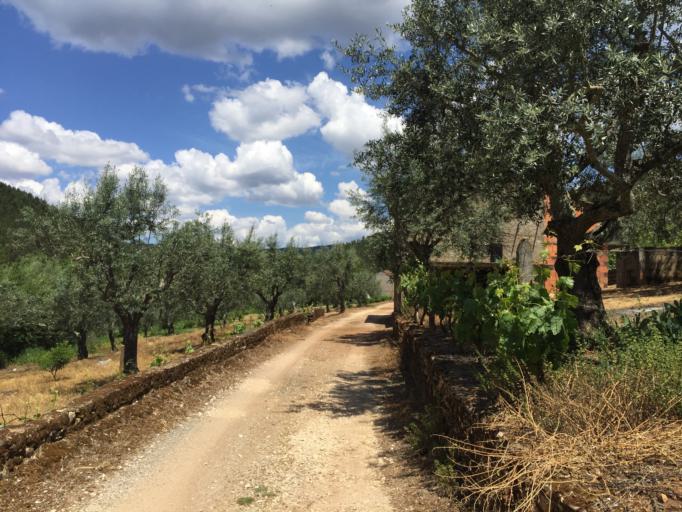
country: PT
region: Coimbra
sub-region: Pampilhosa da Serra
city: Pampilhosa da Serra
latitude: 40.0734
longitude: -7.7850
